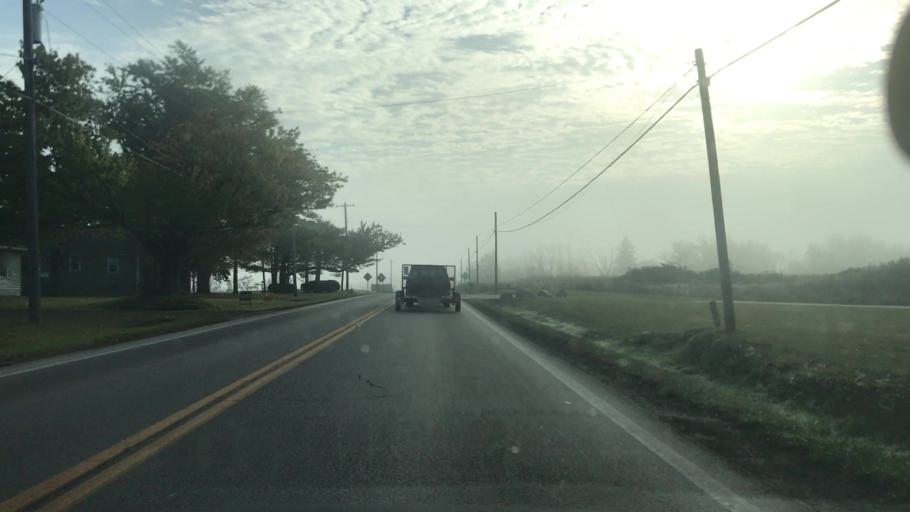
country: US
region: Ohio
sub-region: Geauga County
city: Middlefield
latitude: 41.4604
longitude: -81.0489
